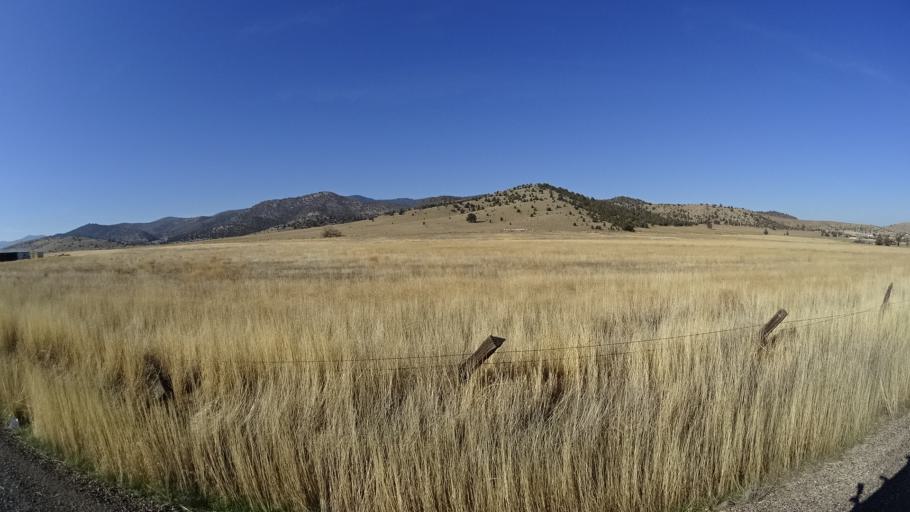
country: US
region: California
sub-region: Siskiyou County
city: Montague
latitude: 41.6244
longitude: -122.5298
